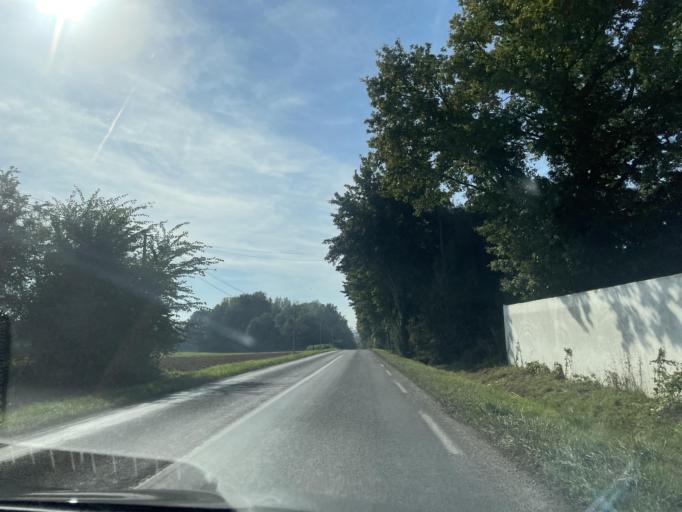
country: FR
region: Ile-de-France
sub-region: Departement de Seine-et-Marne
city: Coulommiers
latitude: 48.8487
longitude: 3.0900
